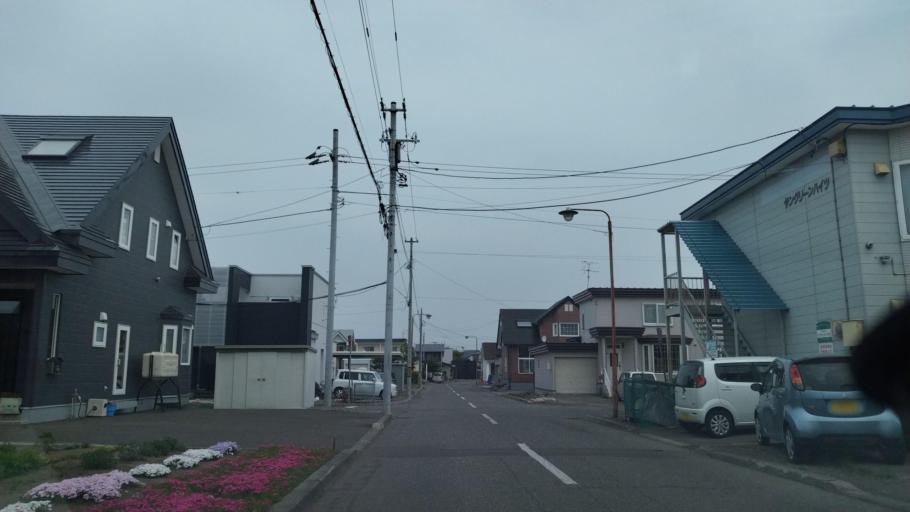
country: JP
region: Hokkaido
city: Obihiro
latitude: 42.9131
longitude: 143.0608
